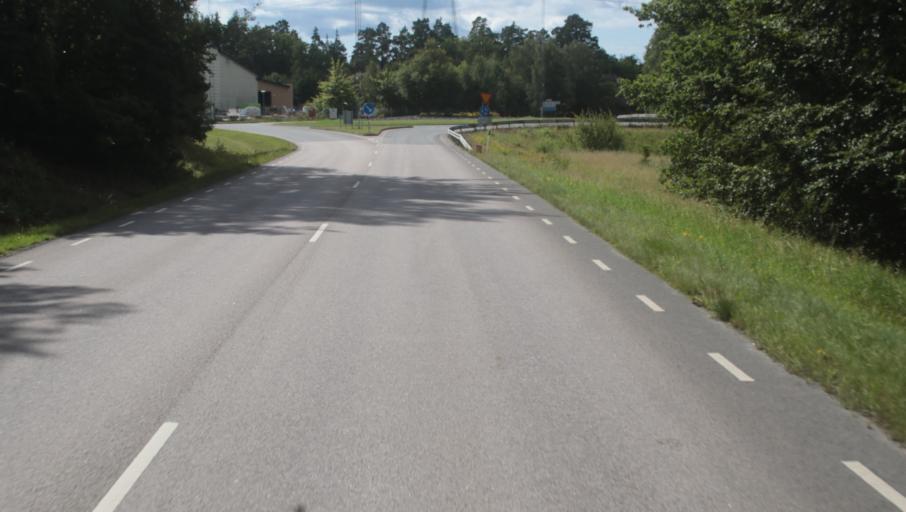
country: SE
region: Blekinge
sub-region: Karlshamns Kommun
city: Karlshamn
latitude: 56.1764
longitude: 14.8385
